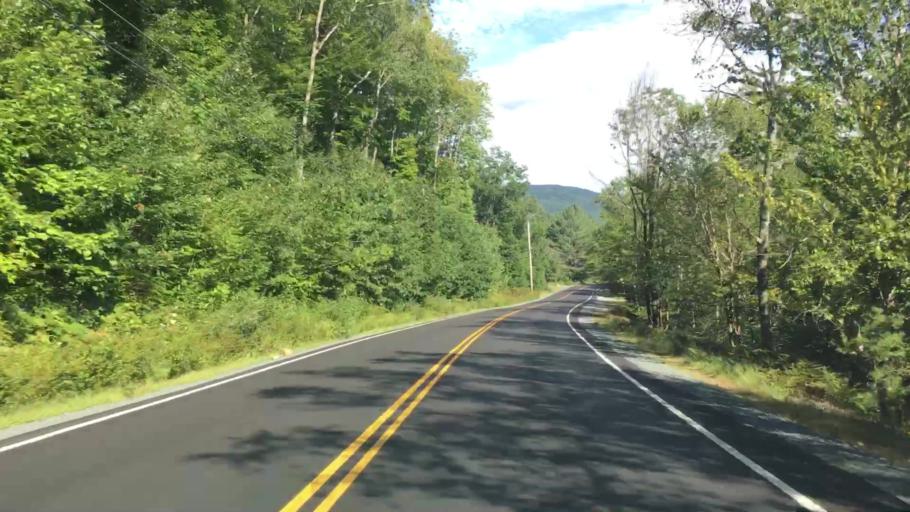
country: US
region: New Hampshire
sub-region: Grafton County
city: Woodstock
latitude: 44.0294
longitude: -71.7113
